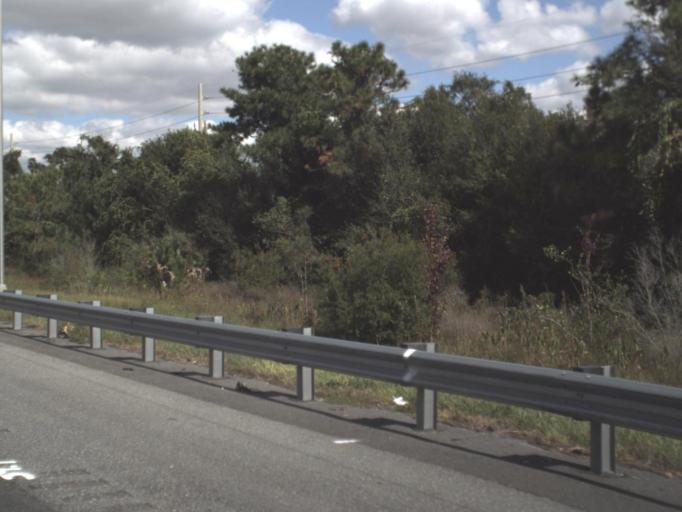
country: US
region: Florida
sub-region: Osceola County
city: Buenaventura Lakes
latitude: 28.3336
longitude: -81.3773
